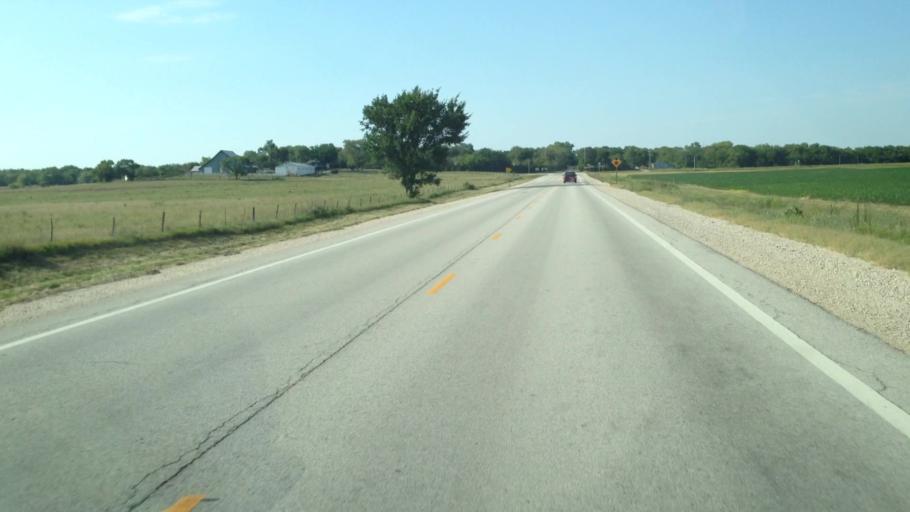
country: US
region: Kansas
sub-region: Anderson County
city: Garnett
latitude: 38.0769
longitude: -95.1694
